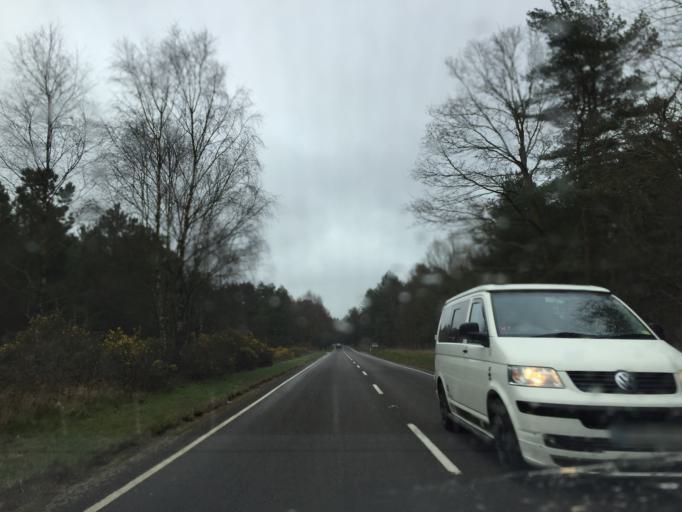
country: GB
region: England
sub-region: Dorset
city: St Leonards
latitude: 50.8609
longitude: -1.8316
